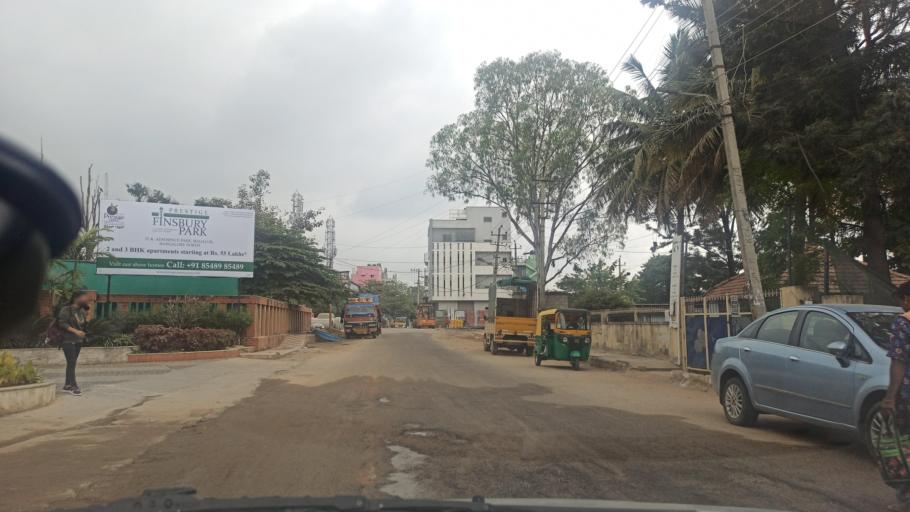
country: IN
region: Karnataka
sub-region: Bangalore Urban
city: Yelahanka
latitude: 13.0464
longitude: 77.6012
